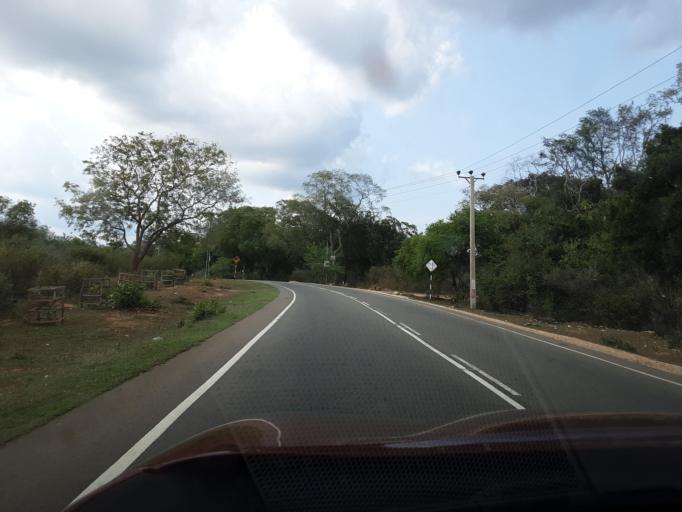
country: LK
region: Uva
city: Haputale
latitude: 6.5040
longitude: 81.1315
